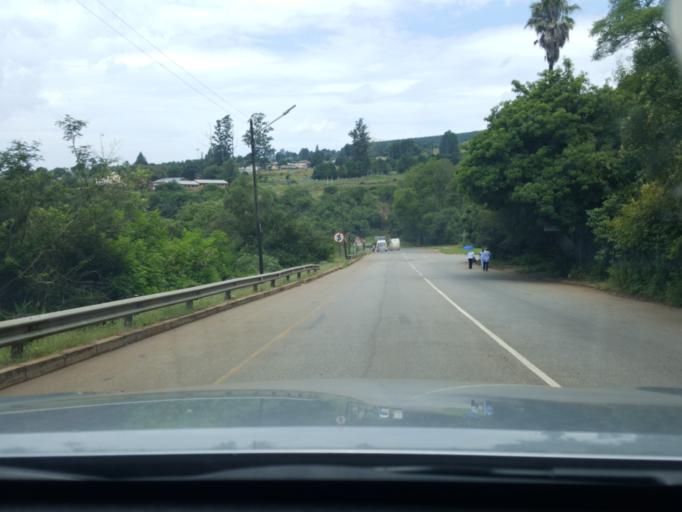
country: ZA
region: Mpumalanga
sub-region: Ehlanzeni District
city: Graksop
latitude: -25.1001
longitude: 30.7821
